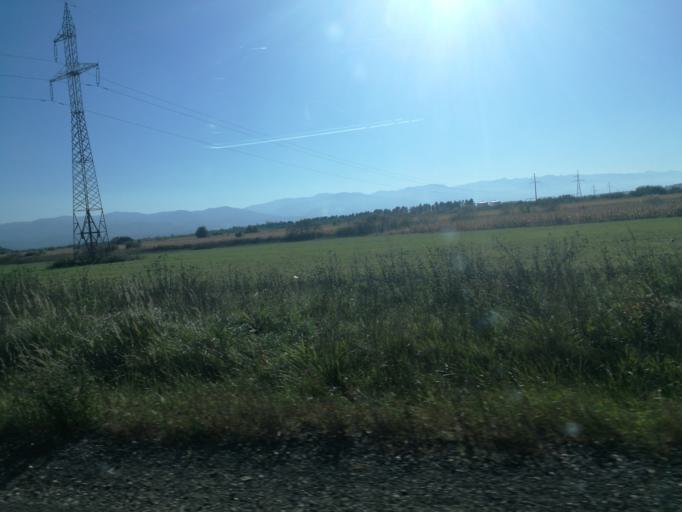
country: RO
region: Brasov
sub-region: Comuna Sercaia
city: Sercaia
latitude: 45.8244
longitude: 25.1556
